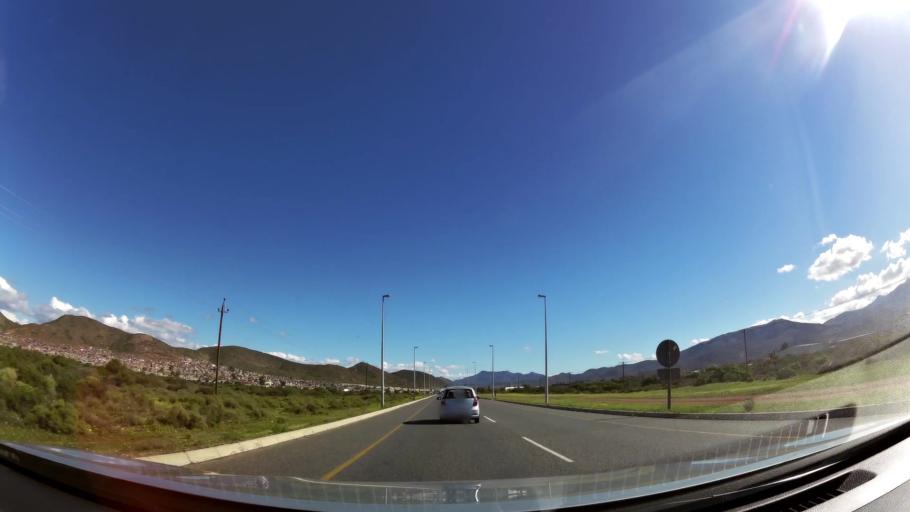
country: ZA
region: Western Cape
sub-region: Cape Winelands District Municipality
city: Ashton
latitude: -33.8148
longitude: 19.9043
